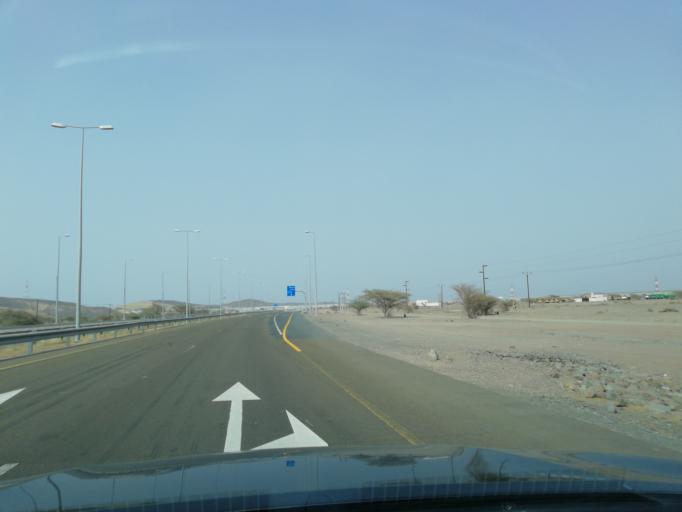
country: OM
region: Al Batinah
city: Al Liwa'
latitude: 24.3761
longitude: 56.5393
